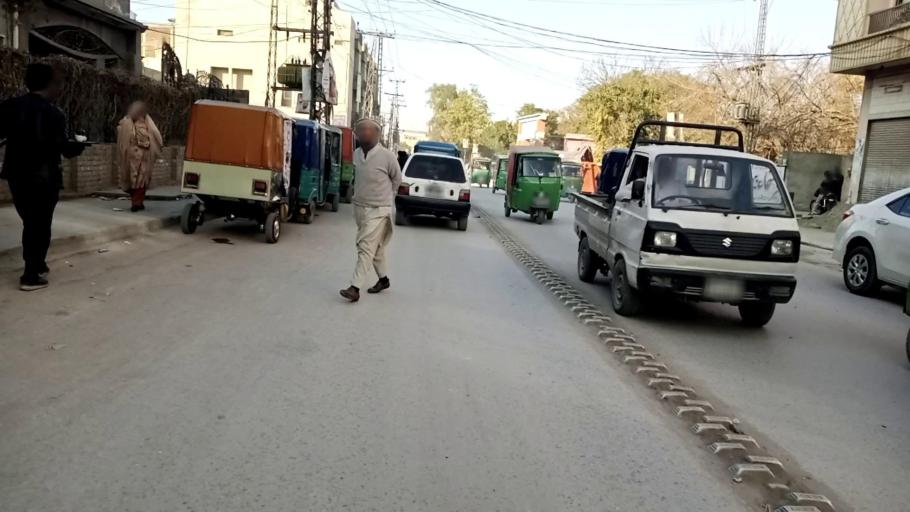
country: PK
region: Khyber Pakhtunkhwa
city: Peshawar
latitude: 34.0121
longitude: 71.5919
